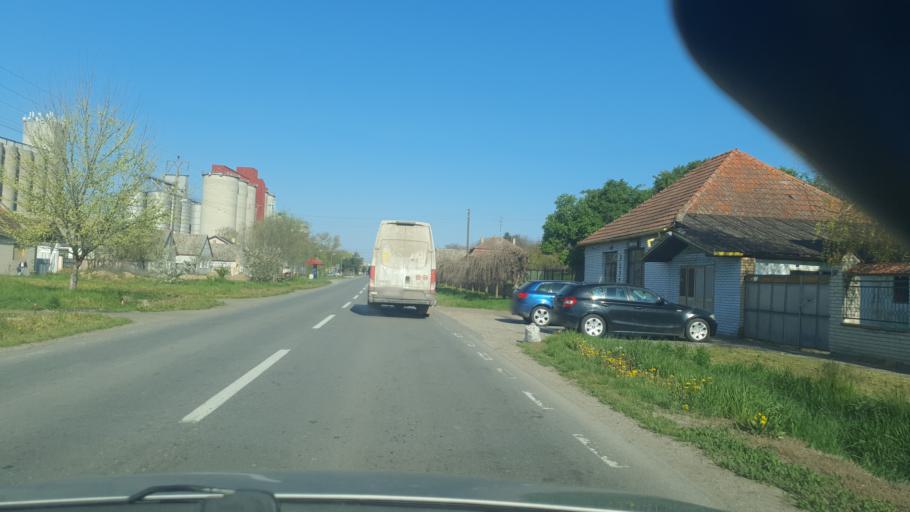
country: RS
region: Autonomna Pokrajina Vojvodina
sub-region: Zapadnobacki Okrug
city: Kula
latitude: 45.6905
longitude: 19.3856
